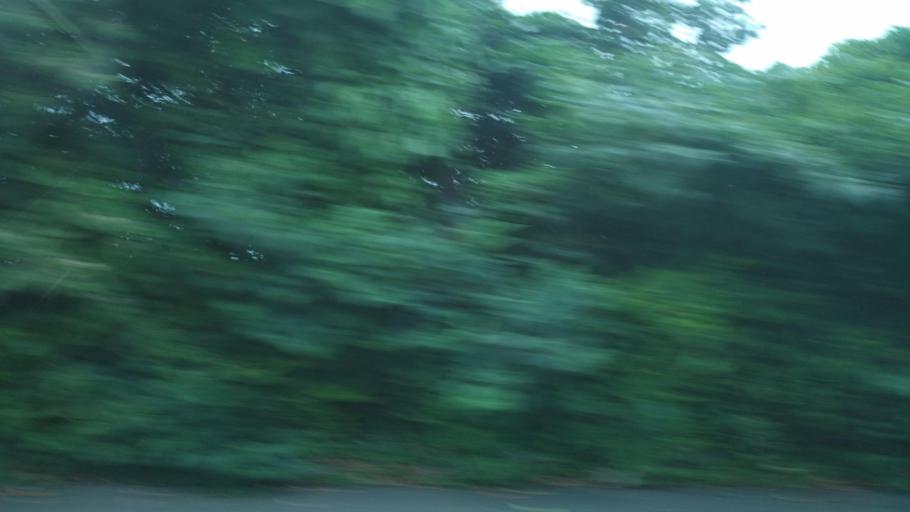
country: TW
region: Taiwan
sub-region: Keelung
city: Keelung
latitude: 25.2206
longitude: 121.6469
